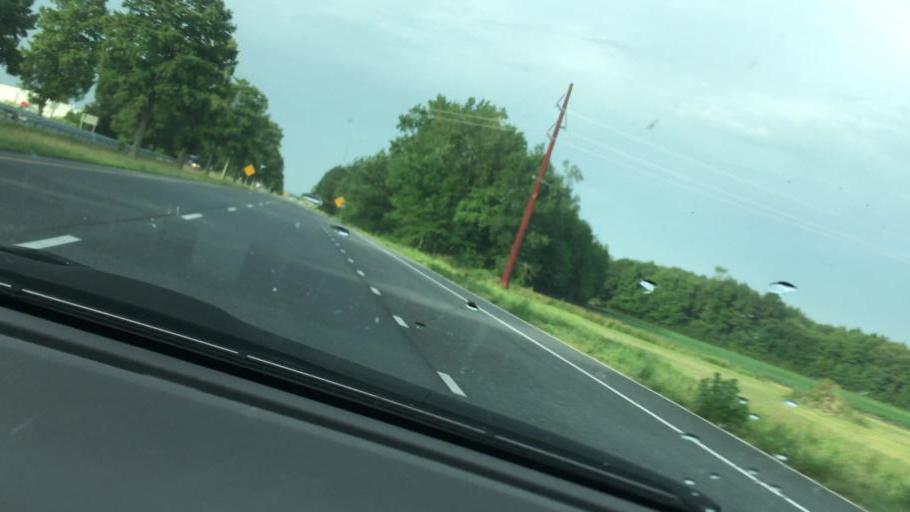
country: US
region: Maryland
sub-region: Wicomico County
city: Fruitland
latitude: 38.3140
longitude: -75.6258
